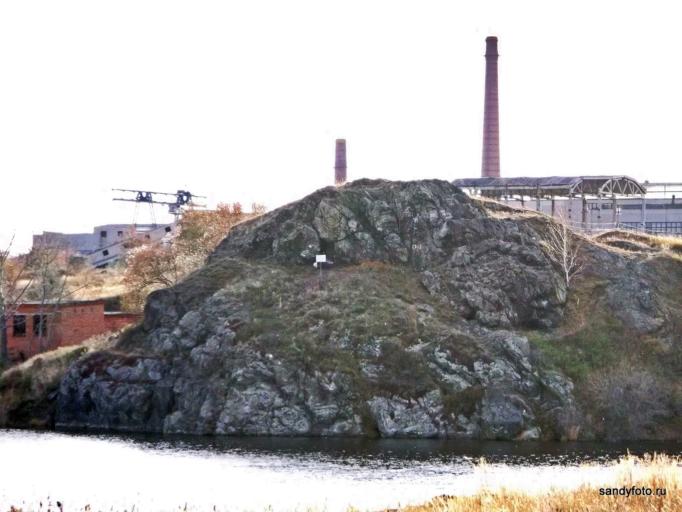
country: RU
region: Chelyabinsk
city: Troitsk
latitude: 54.0737
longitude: 61.5813
